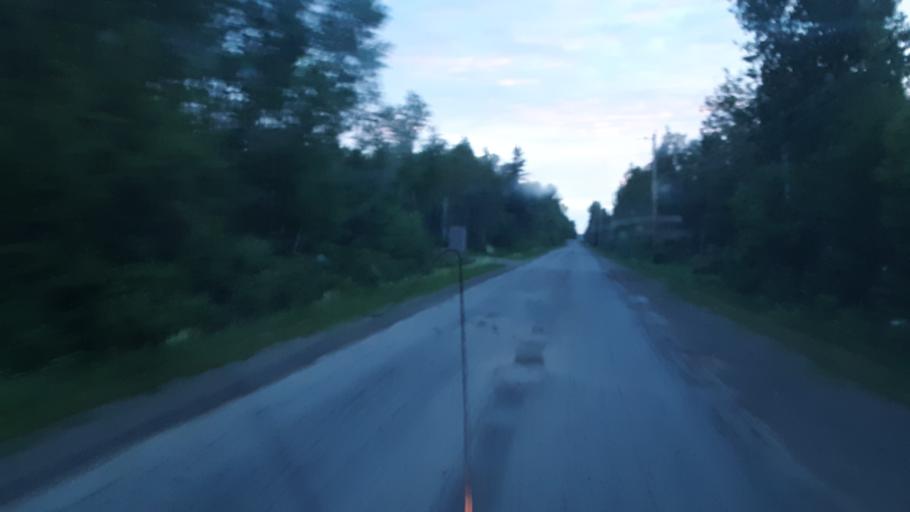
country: US
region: Maine
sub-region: Aroostook County
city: Caribou
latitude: 46.8457
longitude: -68.0917
